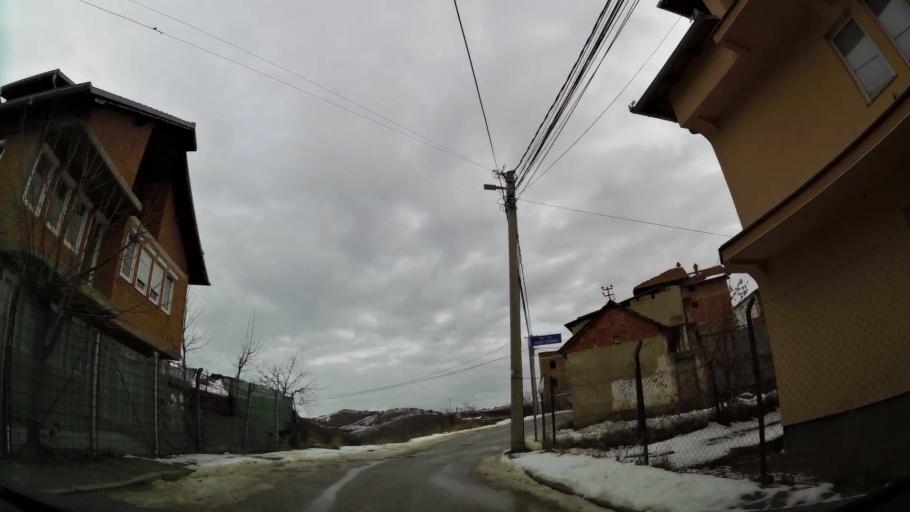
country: XK
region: Pristina
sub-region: Komuna e Prishtines
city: Pristina
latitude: 42.6896
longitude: 21.1718
